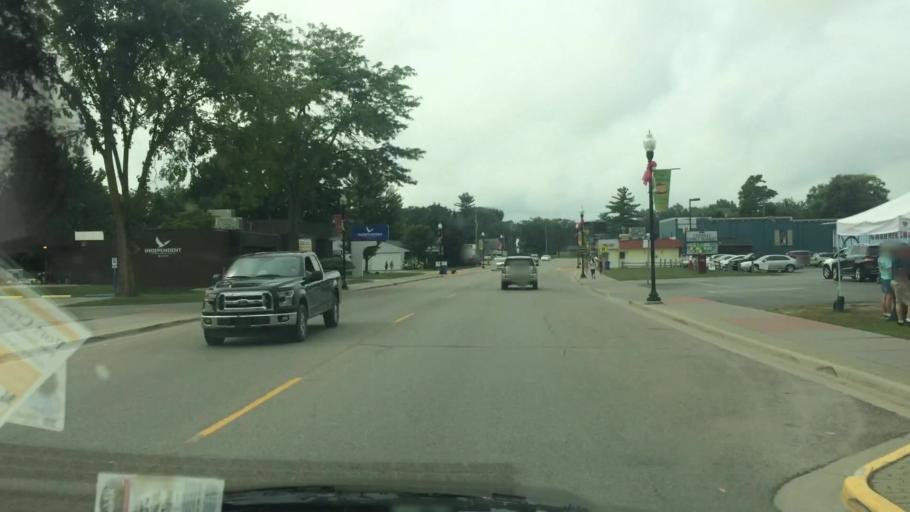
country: US
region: Michigan
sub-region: Huron County
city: Pigeon
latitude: 43.9403
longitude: -83.2724
